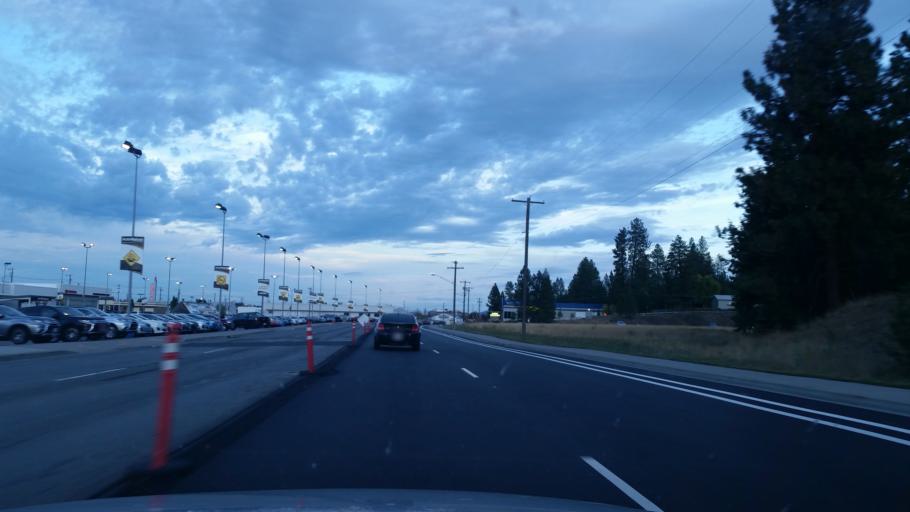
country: US
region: Washington
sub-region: Spokane County
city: Dishman
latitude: 47.6550
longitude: -117.2922
